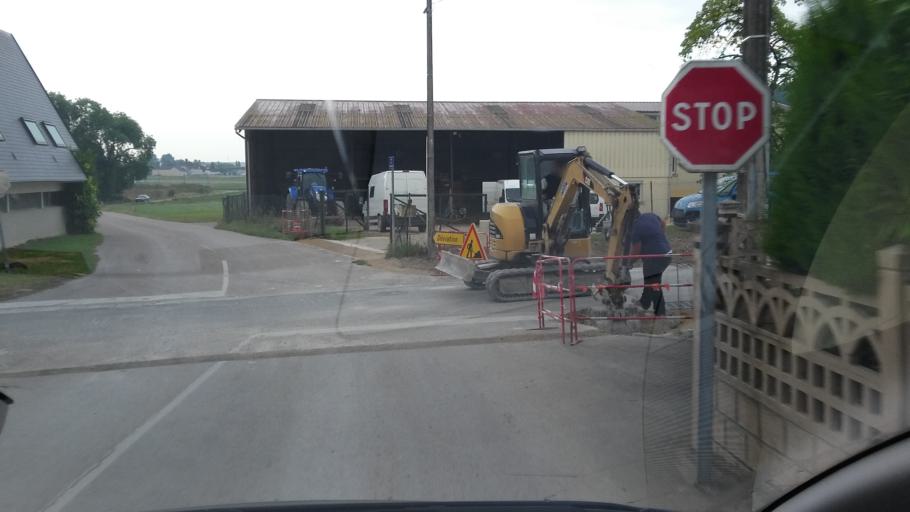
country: FR
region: Champagne-Ardenne
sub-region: Departement de la Marne
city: Vertus
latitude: 48.8812
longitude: 4.0006
